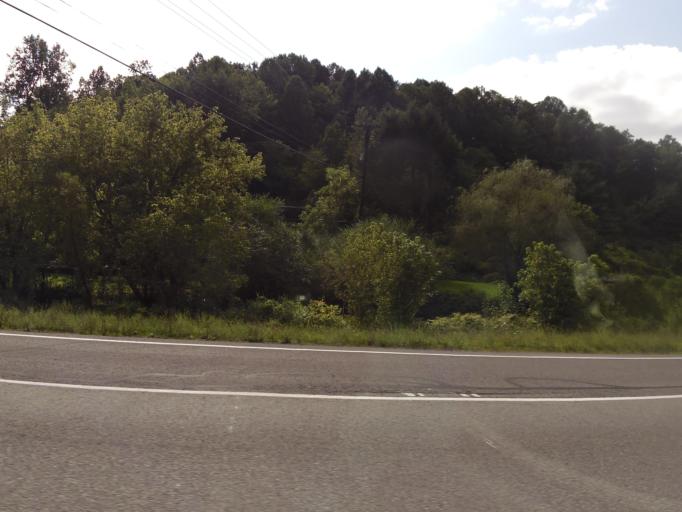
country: US
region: Kentucky
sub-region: Bell County
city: Pineville
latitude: 36.7001
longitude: -83.6934
